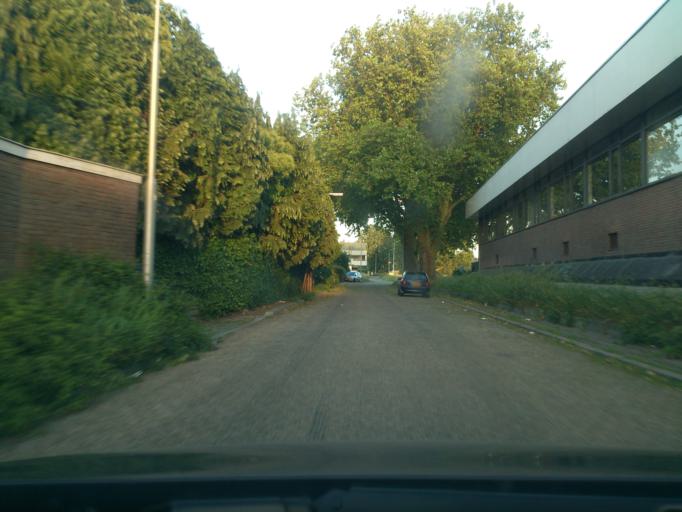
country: NL
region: Gelderland
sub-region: Gemeente Nijmegen
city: Nijmegen
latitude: 51.8526
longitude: 5.8493
